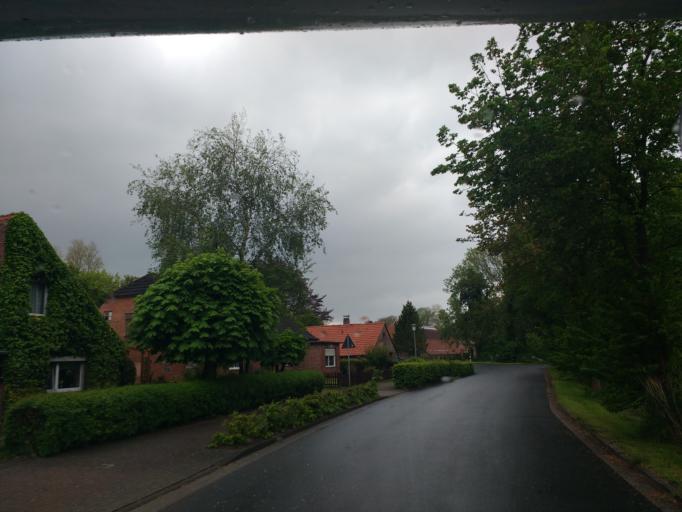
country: DE
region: Lower Saxony
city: Wangerooge
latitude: 53.6976
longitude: 7.8998
